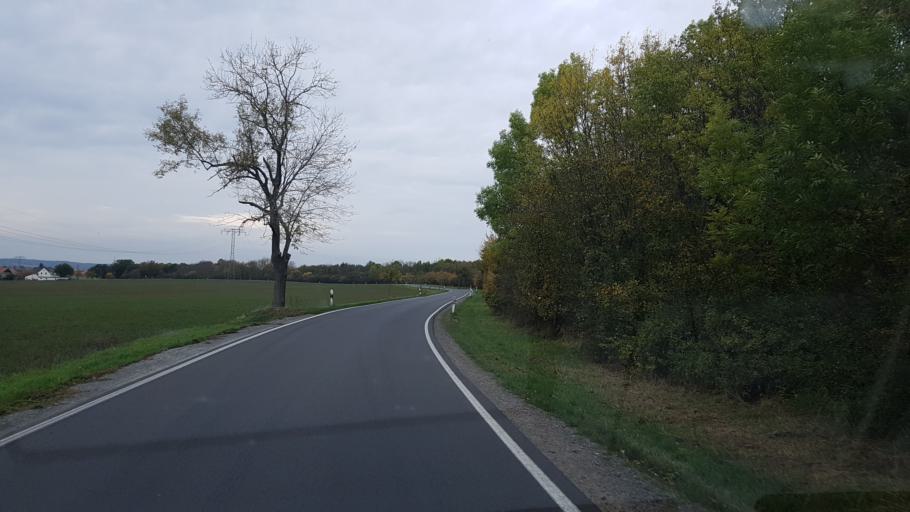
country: DE
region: Saxony
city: Falkenhain
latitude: 51.3838
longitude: 12.9003
